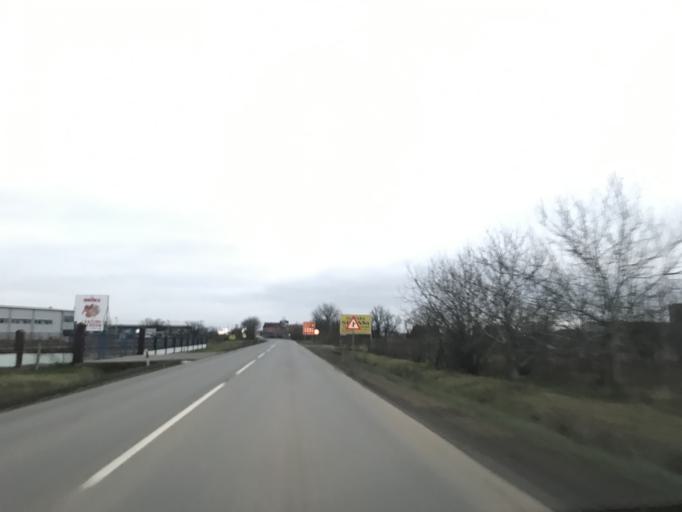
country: RS
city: Rumenka
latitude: 45.2847
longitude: 19.7652
